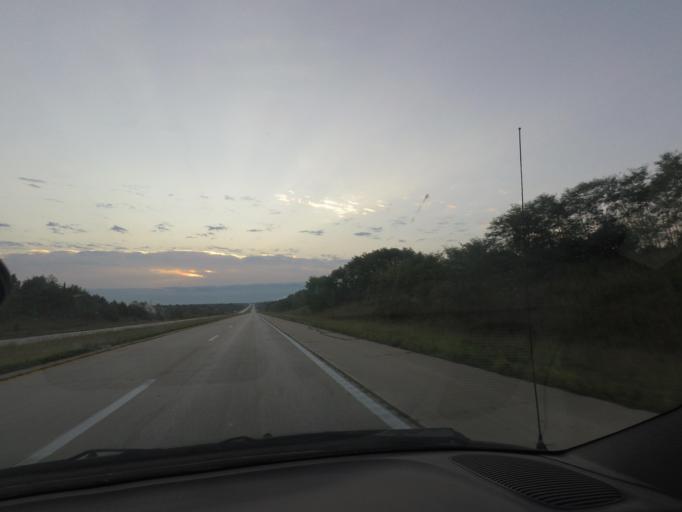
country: US
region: Missouri
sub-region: Macon County
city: Macon
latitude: 39.7545
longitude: -92.4281
